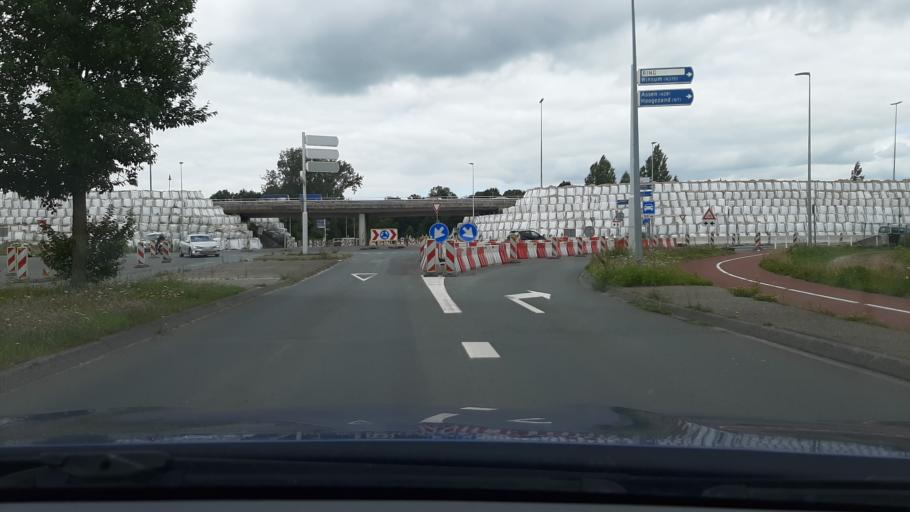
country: NL
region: Groningen
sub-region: Gemeente Groningen
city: Groningen
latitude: 53.1977
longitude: 6.5472
